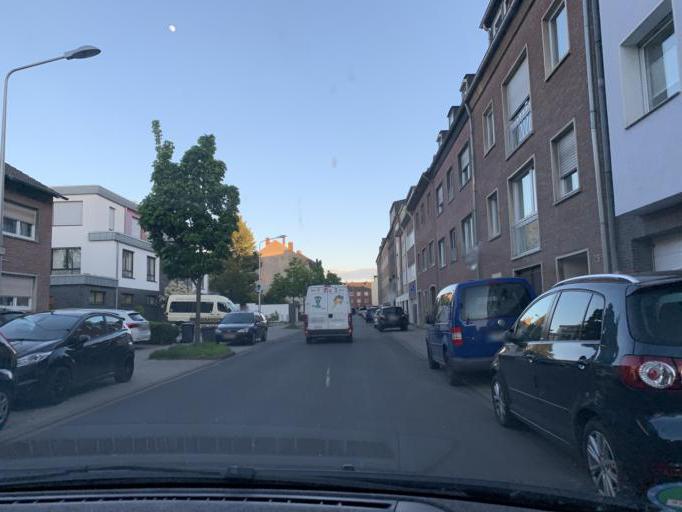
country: DE
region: North Rhine-Westphalia
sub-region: Regierungsbezirk Koln
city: Dueren
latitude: 50.8077
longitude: 6.4955
